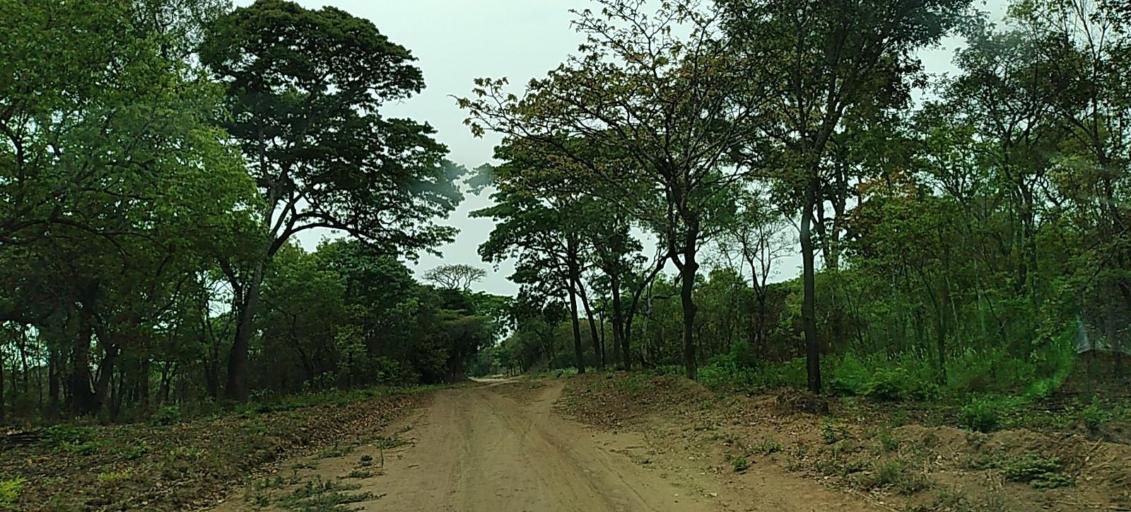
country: ZM
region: North-Western
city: Solwezi
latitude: -12.5279
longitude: 26.5230
